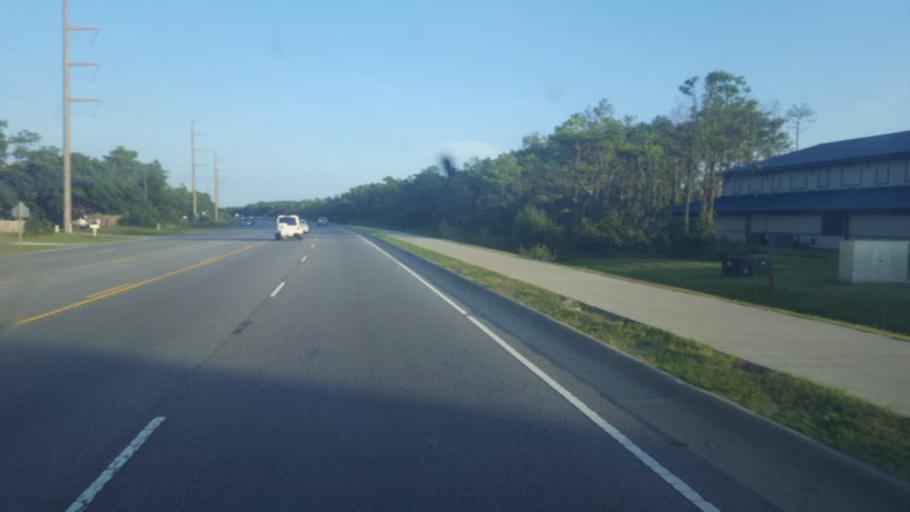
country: US
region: North Carolina
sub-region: Dare County
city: Nags Head
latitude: 35.9739
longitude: -75.6391
